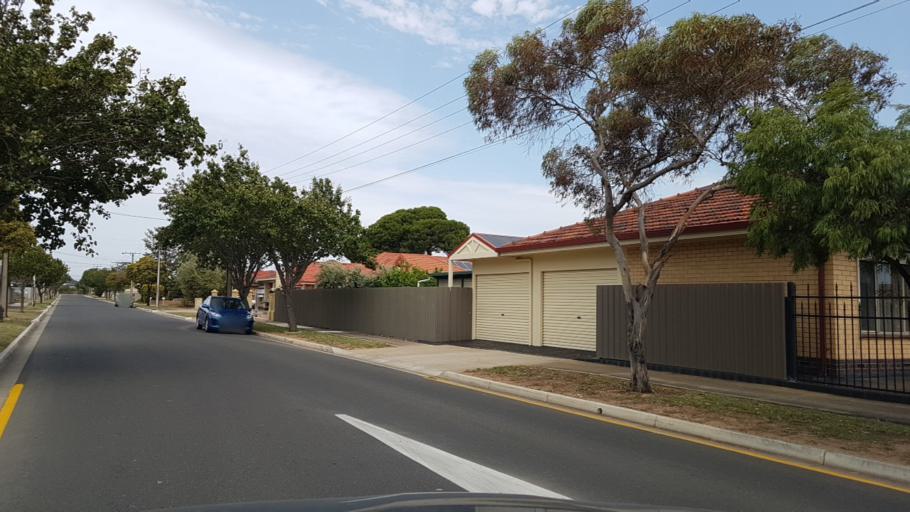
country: AU
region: South Australia
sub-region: Charles Sturt
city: Seaton
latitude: -34.9110
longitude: 138.5094
